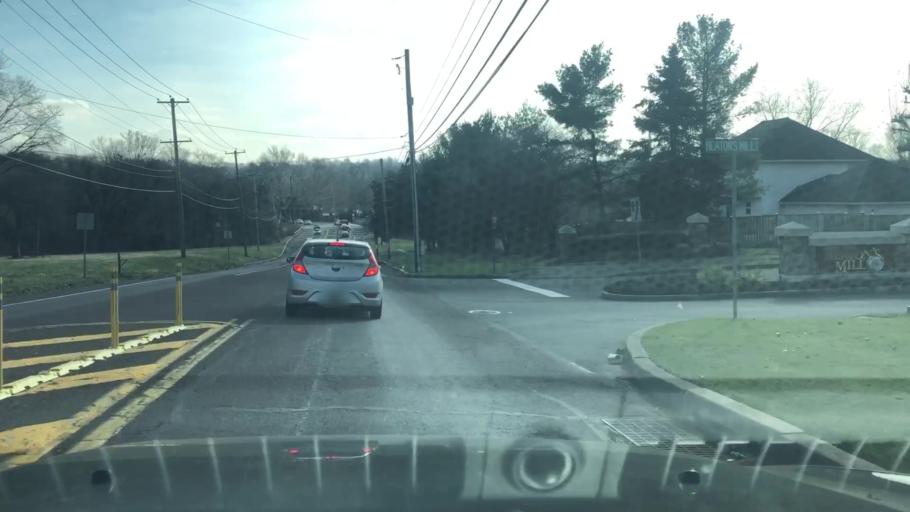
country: US
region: Pennsylvania
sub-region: Bucks County
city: Langhorne
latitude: 40.1928
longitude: -74.9282
